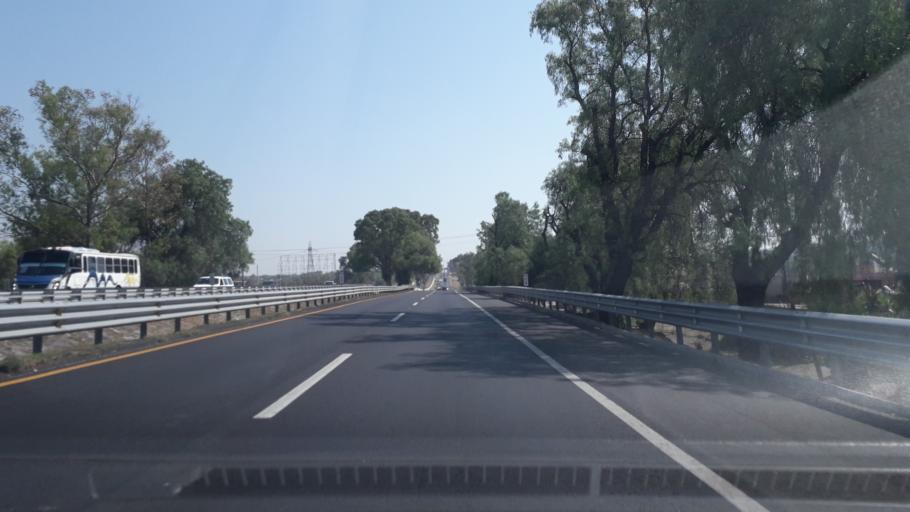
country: MX
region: Mexico
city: Santo Tomas Chiconautla
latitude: 19.6444
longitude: -99.0158
